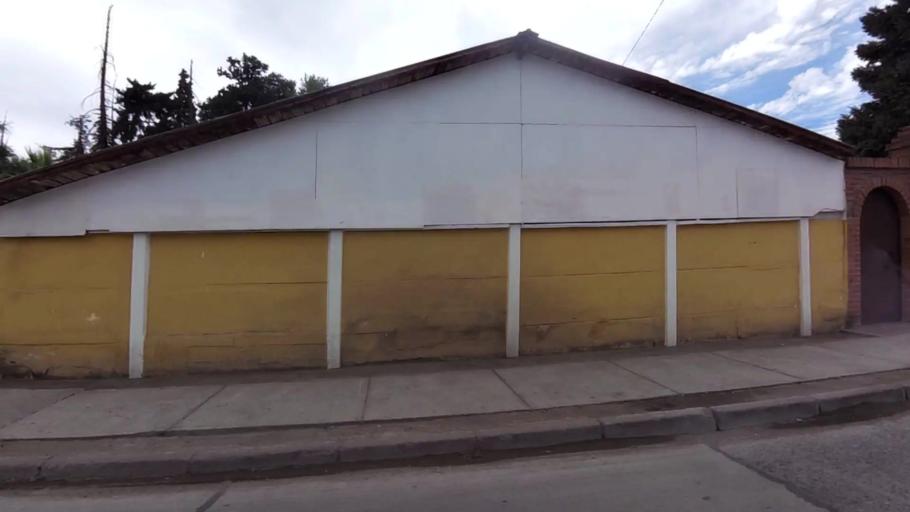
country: CL
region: O'Higgins
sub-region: Provincia de Cachapoal
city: Graneros
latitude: -34.0696
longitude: -70.7206
